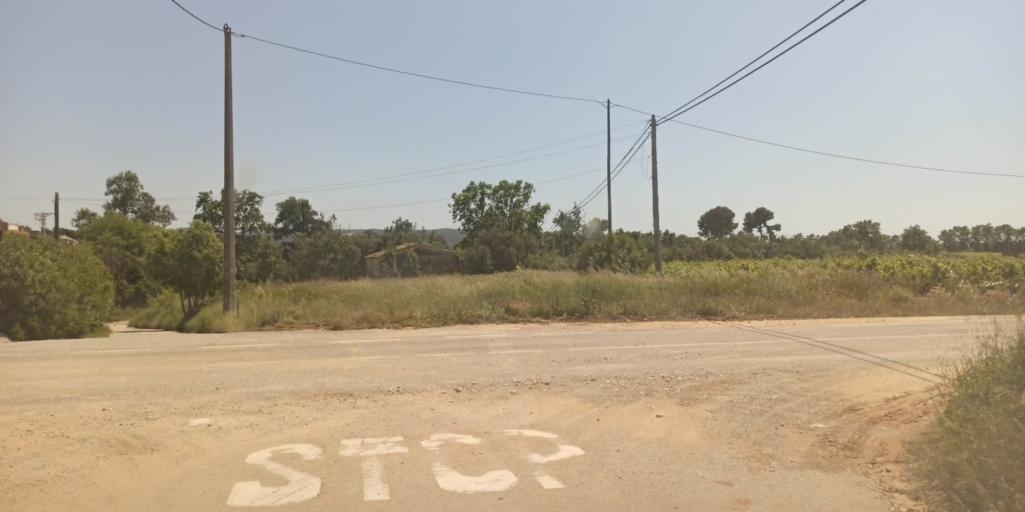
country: ES
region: Catalonia
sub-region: Provincia de Barcelona
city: Vilafranca del Penedes
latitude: 41.3380
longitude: 1.6586
